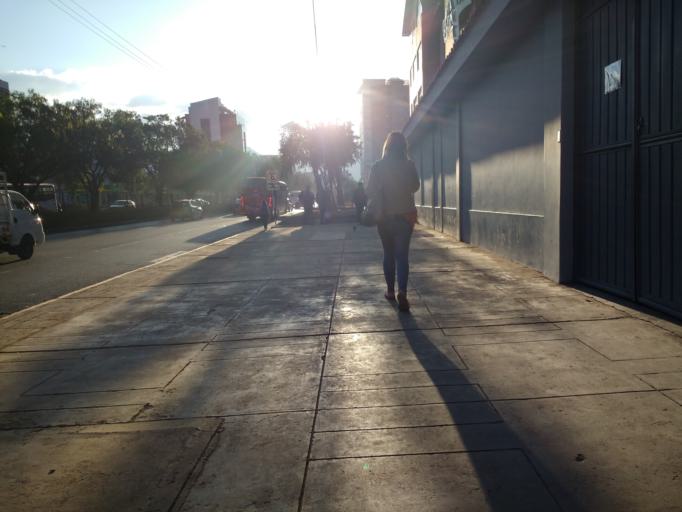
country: PE
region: Cusco
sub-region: Provincia de Cusco
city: Cusco
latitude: -13.5261
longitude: -71.9500
